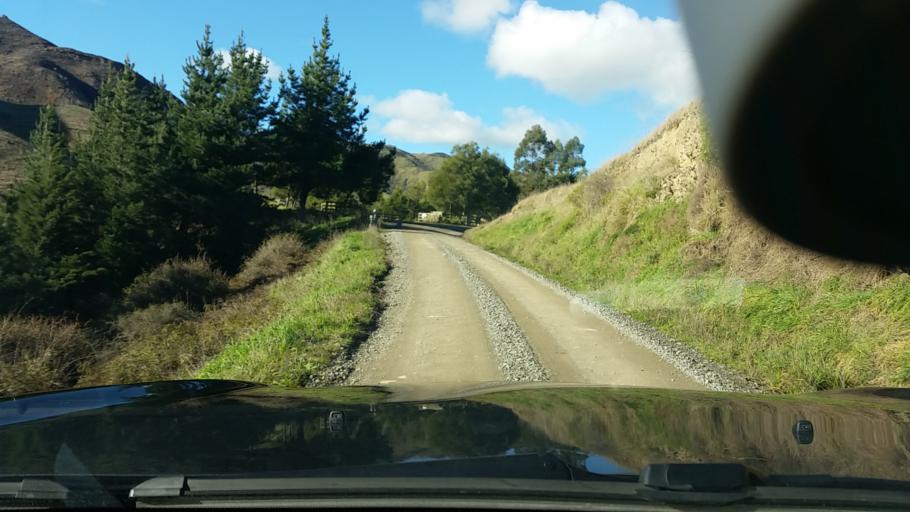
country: NZ
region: Marlborough
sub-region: Marlborough District
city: Blenheim
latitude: -41.6039
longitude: 173.9615
